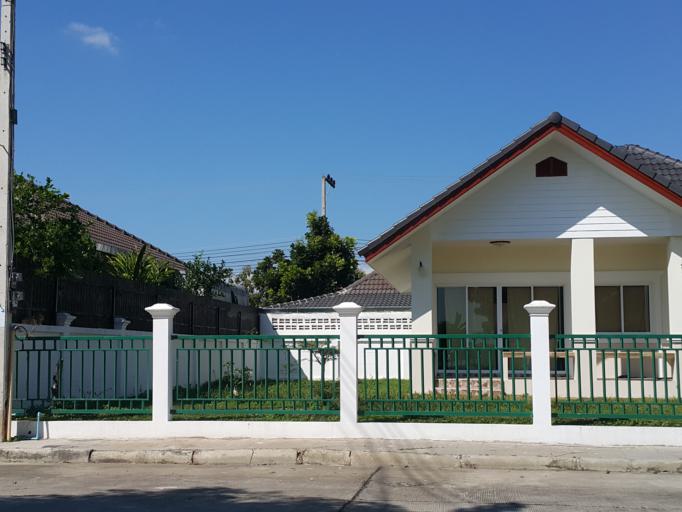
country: TH
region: Chiang Mai
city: San Sai
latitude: 18.9469
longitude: 98.9257
